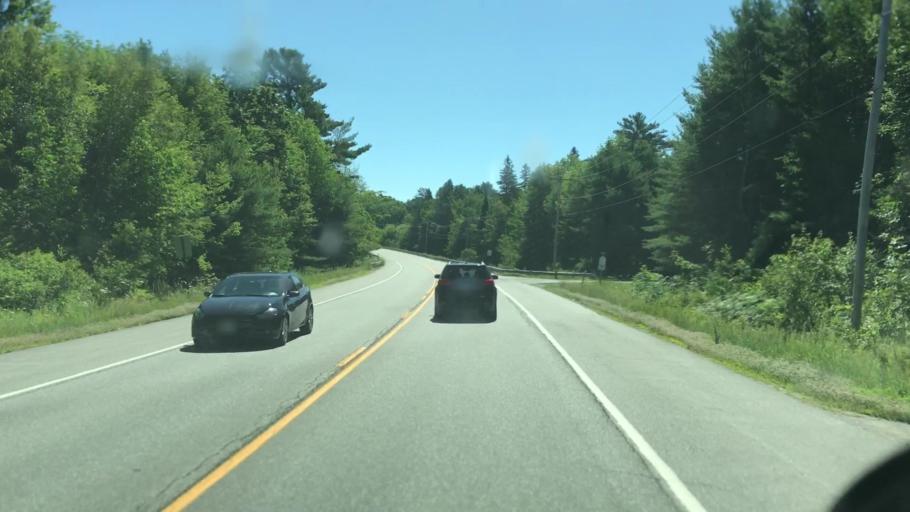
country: US
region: Maine
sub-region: Penobscot County
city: Holden
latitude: 44.7550
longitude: -68.6825
